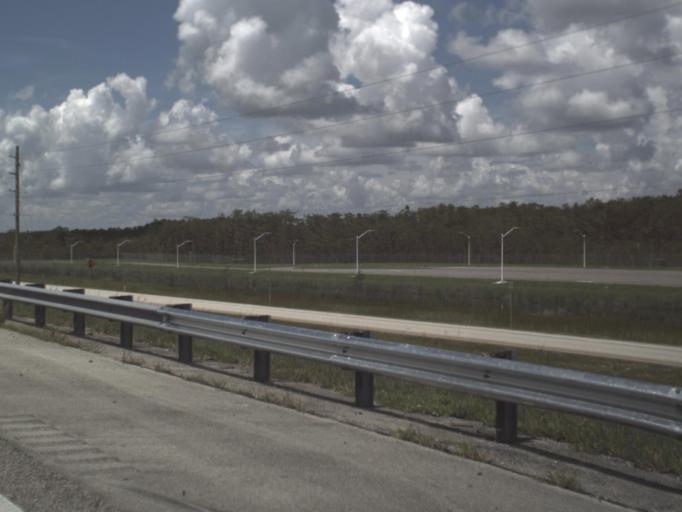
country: US
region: Florida
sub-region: Collier County
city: Immokalee
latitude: 26.1687
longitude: -81.0727
